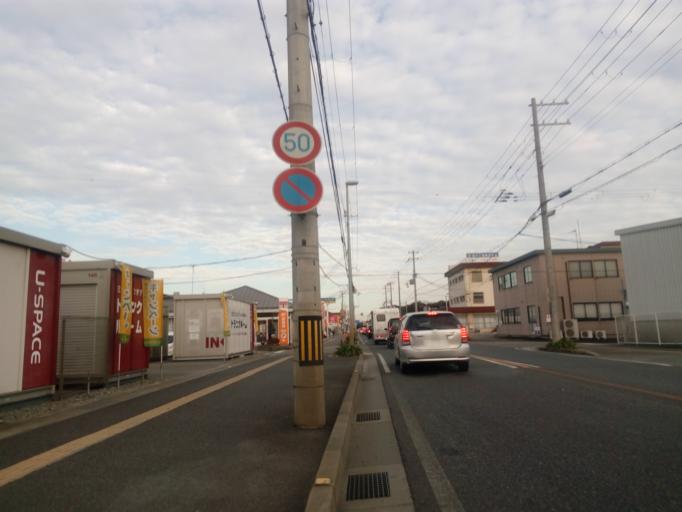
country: JP
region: Hyogo
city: Himeji
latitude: 34.7954
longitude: 134.6340
